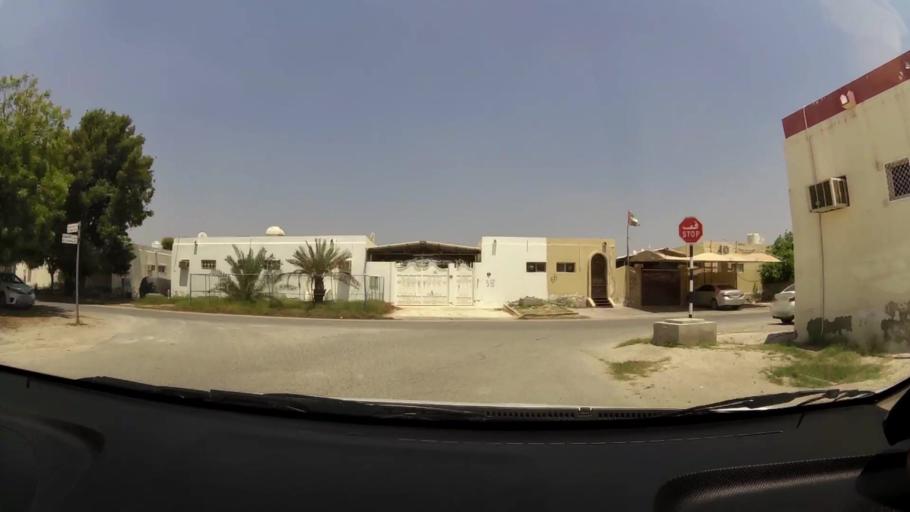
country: AE
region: Umm al Qaywayn
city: Umm al Qaywayn
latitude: 25.5613
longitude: 55.5603
